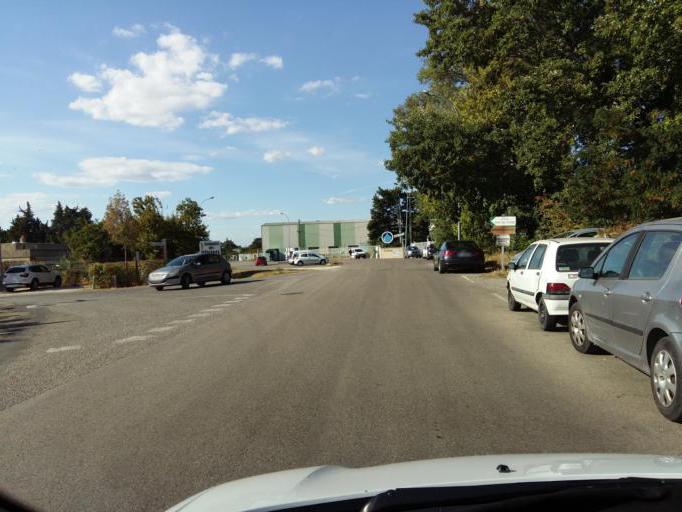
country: FR
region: Provence-Alpes-Cote d'Azur
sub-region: Departement du Vaucluse
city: L'Isle-sur-la-Sorgue
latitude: 43.9205
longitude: 5.0345
